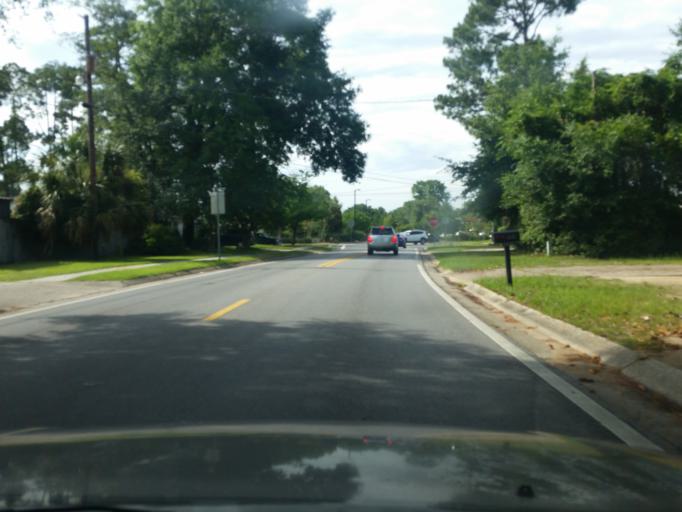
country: US
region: Florida
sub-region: Escambia County
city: Ferry Pass
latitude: 30.4871
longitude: -87.2150
